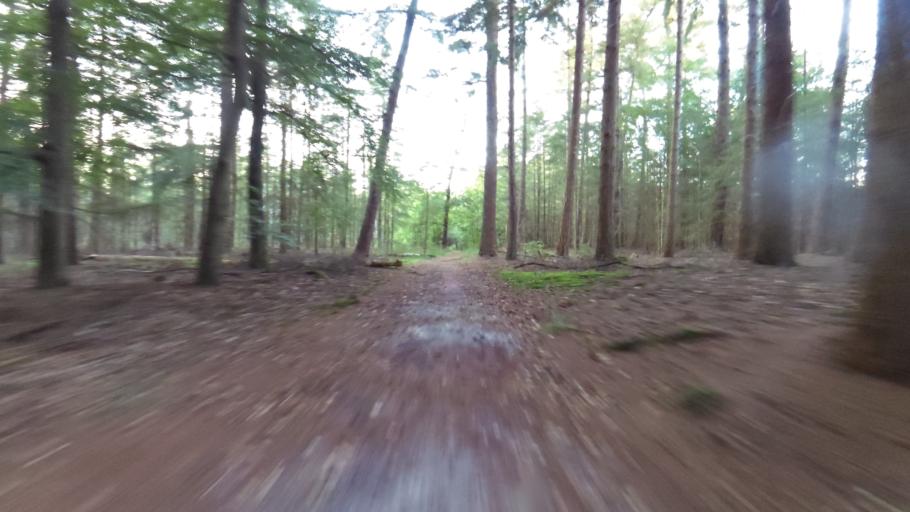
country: NL
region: Utrecht
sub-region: Gemeente Soest
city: Soest
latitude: 52.1568
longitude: 5.2468
